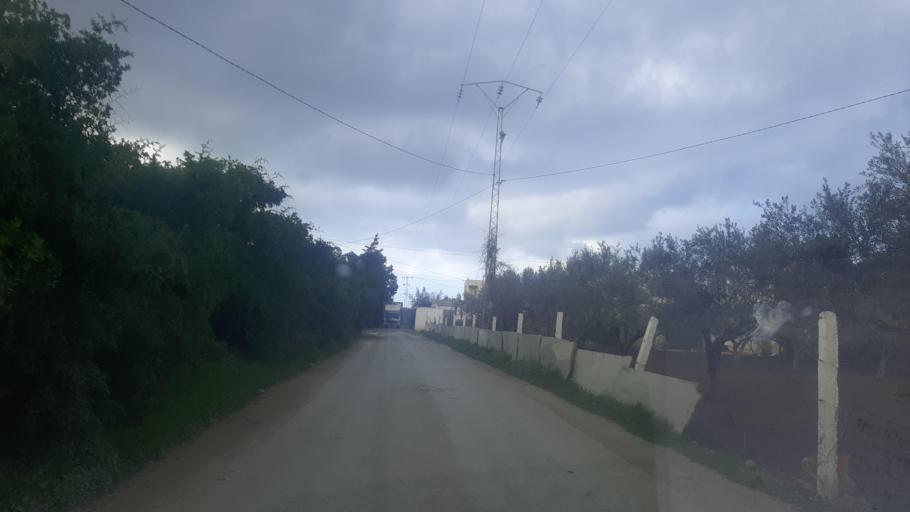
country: TN
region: Nabul
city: Manzil Bu Zalafah
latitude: 36.7347
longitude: 10.5351
